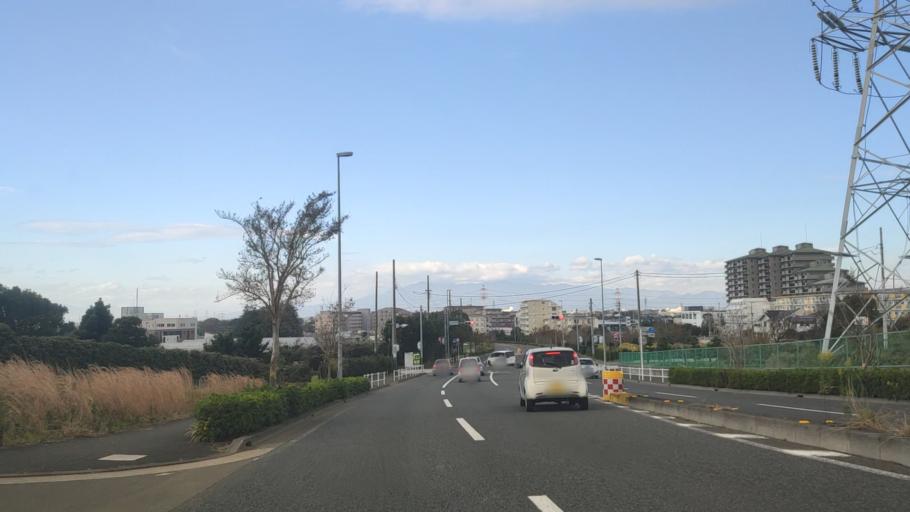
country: JP
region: Kanagawa
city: Minami-rinkan
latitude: 35.4282
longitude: 139.4998
